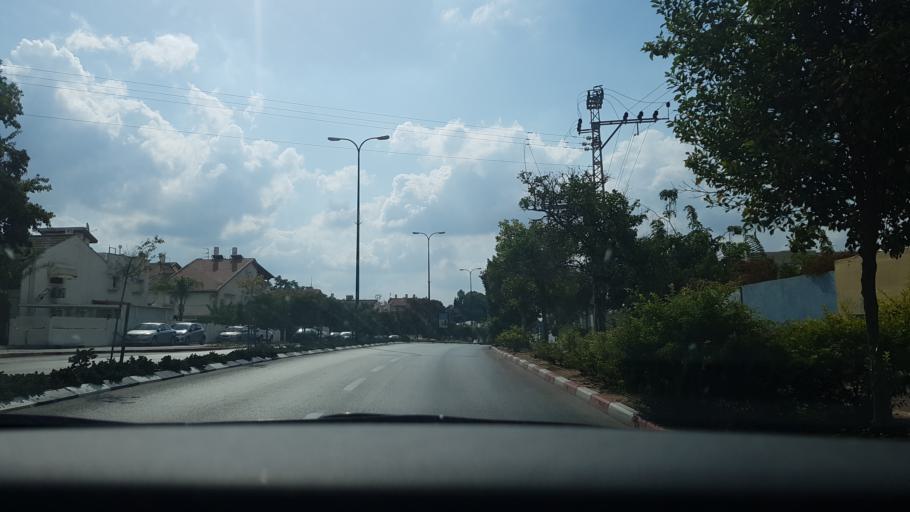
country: IL
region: Central District
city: Mazkeret Batya
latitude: 31.8811
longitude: 34.8176
